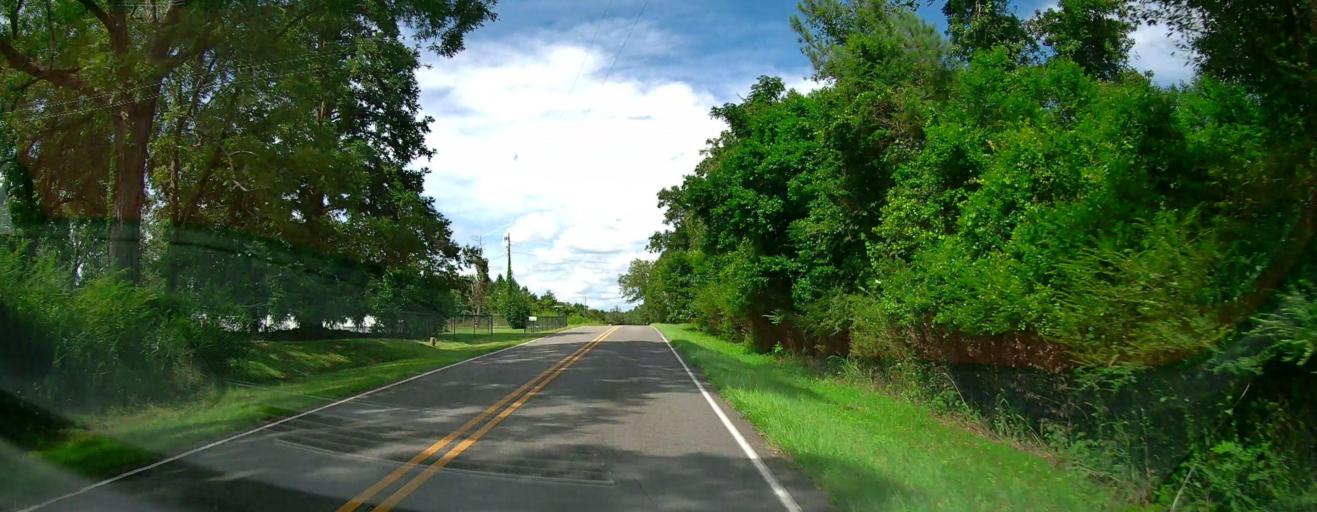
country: US
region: Georgia
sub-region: Taylor County
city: Butler
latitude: 32.4892
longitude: -84.2056
